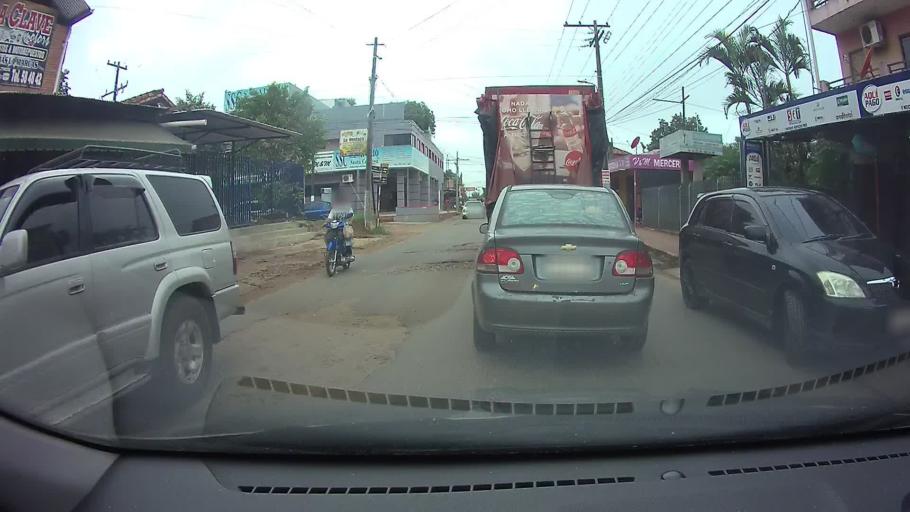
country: PY
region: Central
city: San Lorenzo
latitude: -25.3231
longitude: -57.4988
